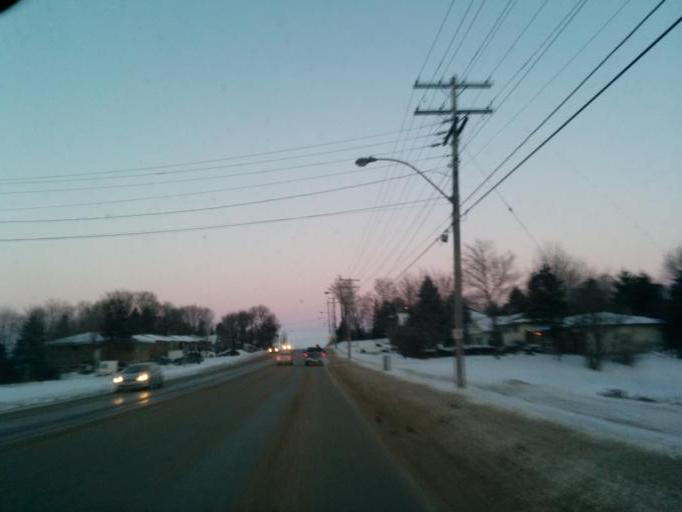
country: CA
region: Ontario
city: Shelburne
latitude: 44.0803
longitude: -80.1949
